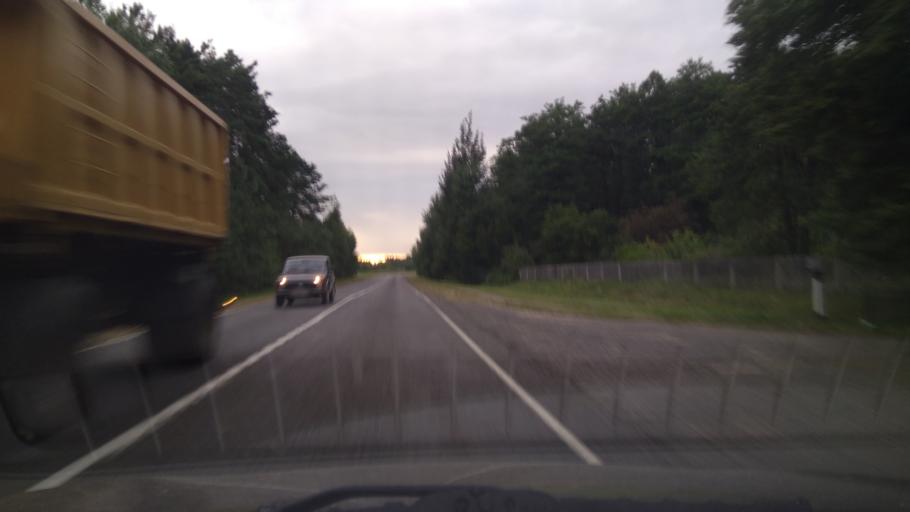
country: BY
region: Brest
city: Byaroza
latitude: 52.4153
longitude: 24.9847
